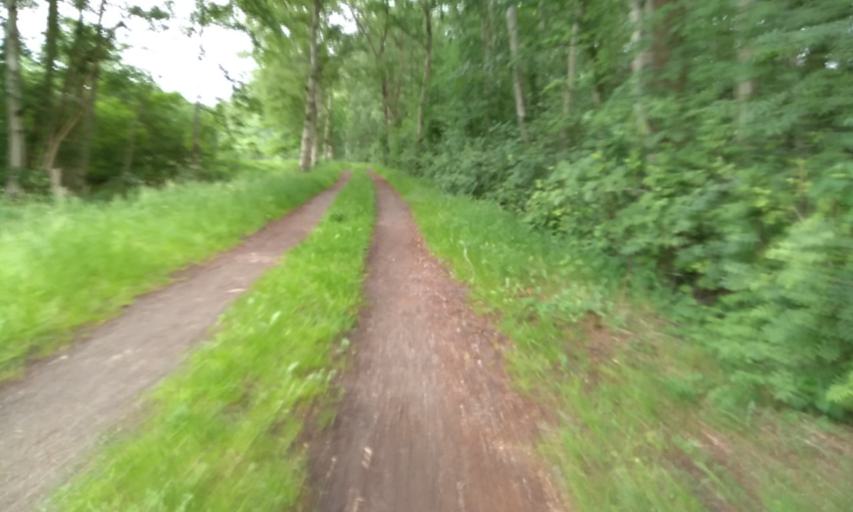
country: DE
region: Lower Saxony
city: Buxtehude
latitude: 53.4907
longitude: 9.6821
